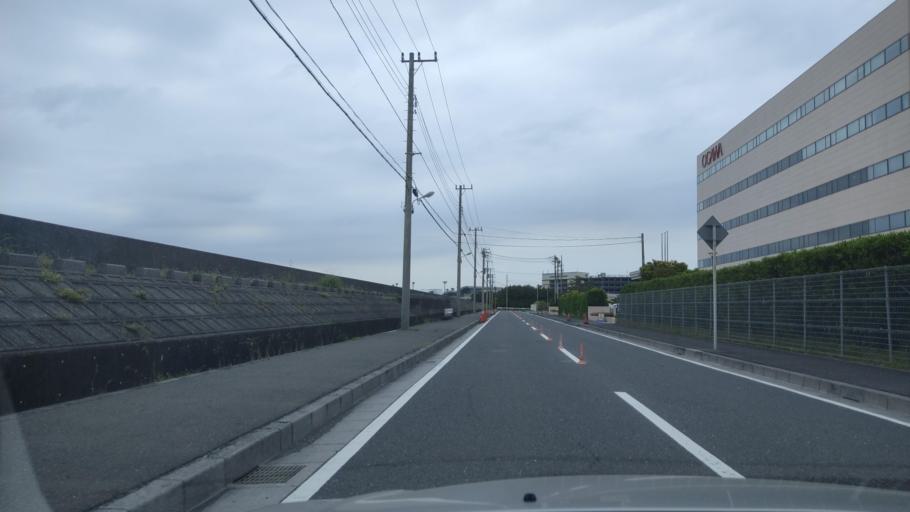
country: JP
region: Tokyo
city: Urayasu
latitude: 35.6211
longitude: 139.8953
